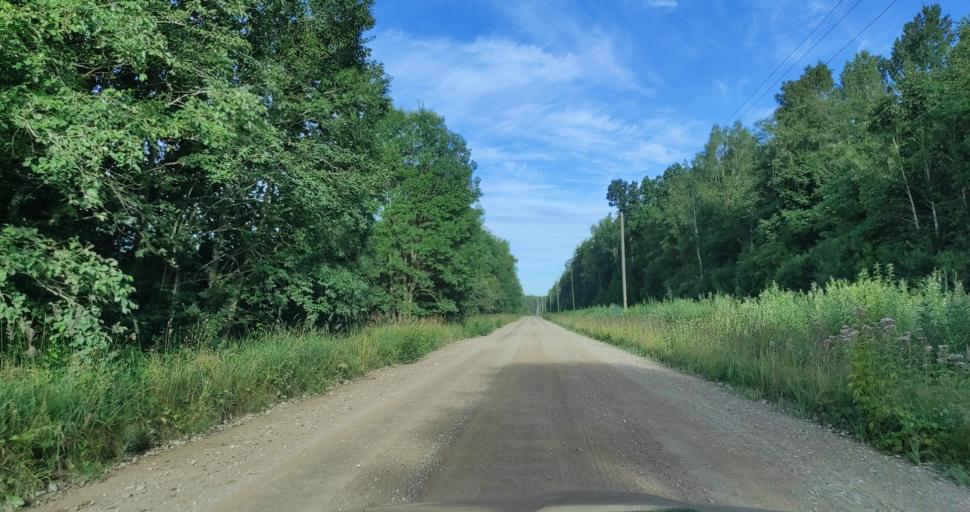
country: LV
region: Durbe
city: Liegi
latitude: 56.7528
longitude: 21.3555
